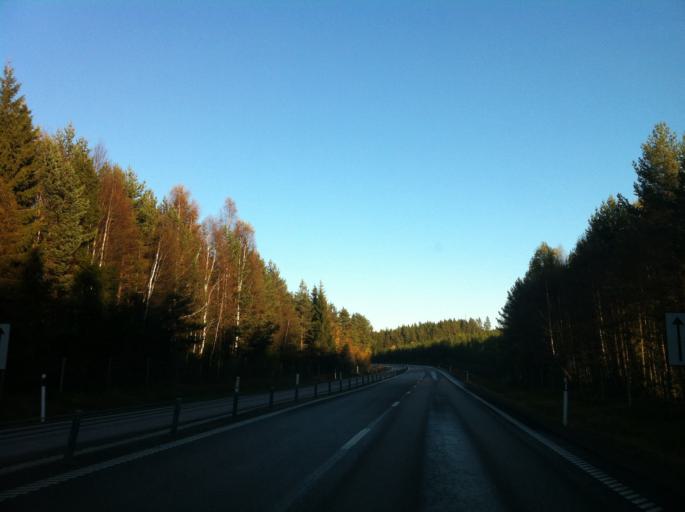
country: SE
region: Dalarna
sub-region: Hedemora Kommun
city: Langshyttan
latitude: 60.5655
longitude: 15.9429
